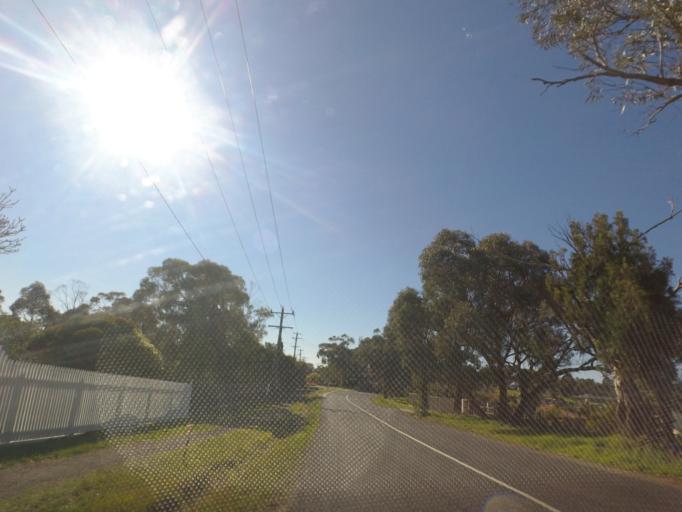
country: AU
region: Victoria
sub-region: Maroondah
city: Croydon Hills
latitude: -37.7421
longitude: 145.2692
